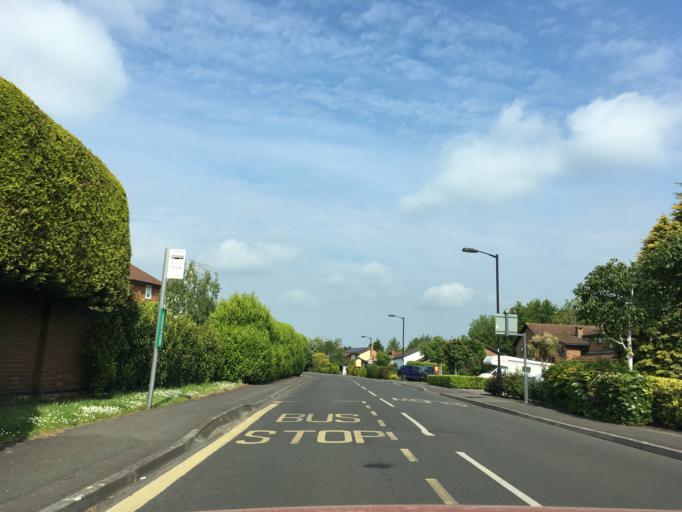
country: GB
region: England
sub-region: North Somerset
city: Nailsea
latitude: 51.4252
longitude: -2.7642
